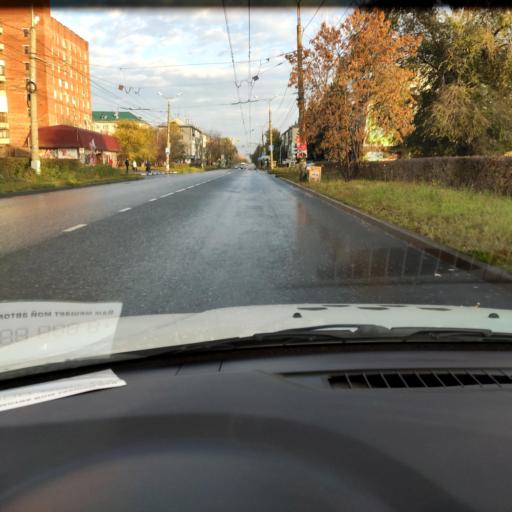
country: RU
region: Samara
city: Tol'yatti
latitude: 53.5207
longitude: 49.4154
